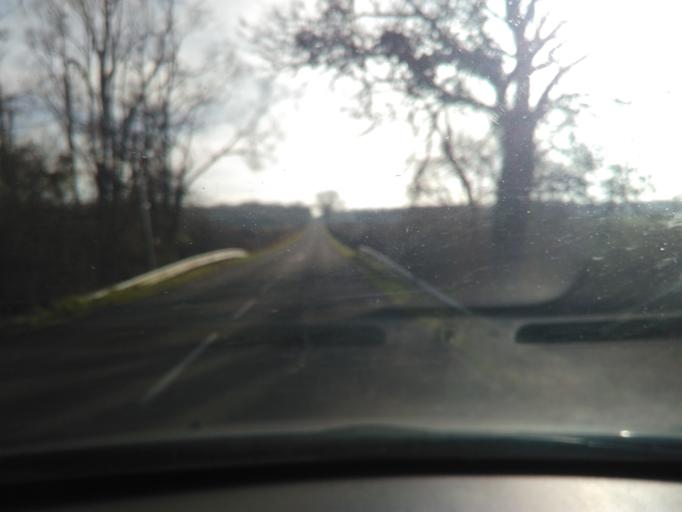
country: FR
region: Bourgogne
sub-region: Departement de la Nievre
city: Dornes
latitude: 46.7797
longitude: 3.2790
